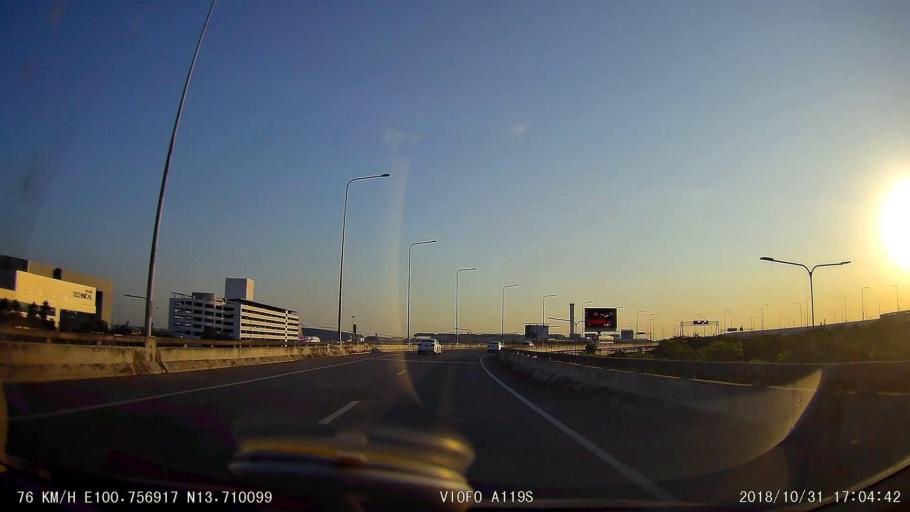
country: TH
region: Bangkok
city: Lat Krabang
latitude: 13.7099
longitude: 100.7567
